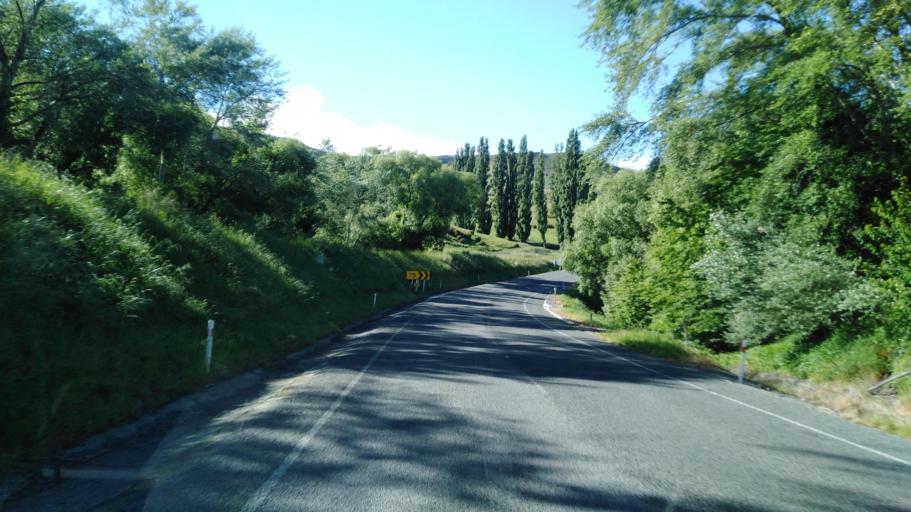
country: NZ
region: Canterbury
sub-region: Hurunui District
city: Amberley
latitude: -42.9864
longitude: 172.7203
